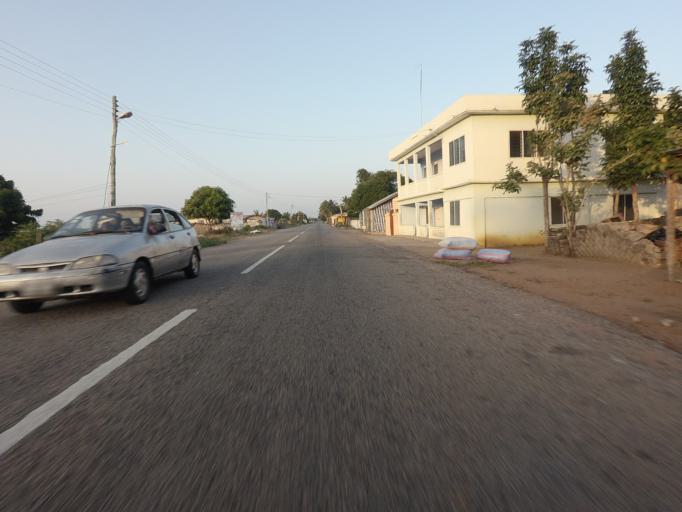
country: GH
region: Volta
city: Anloga
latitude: 5.7828
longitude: 0.8453
